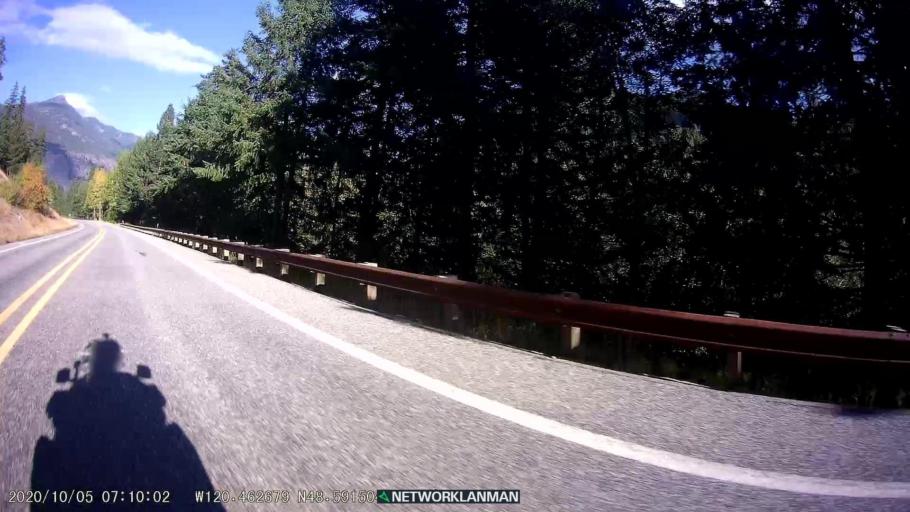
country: US
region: Washington
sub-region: Chelan County
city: Granite Falls
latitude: 48.5915
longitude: -120.4617
